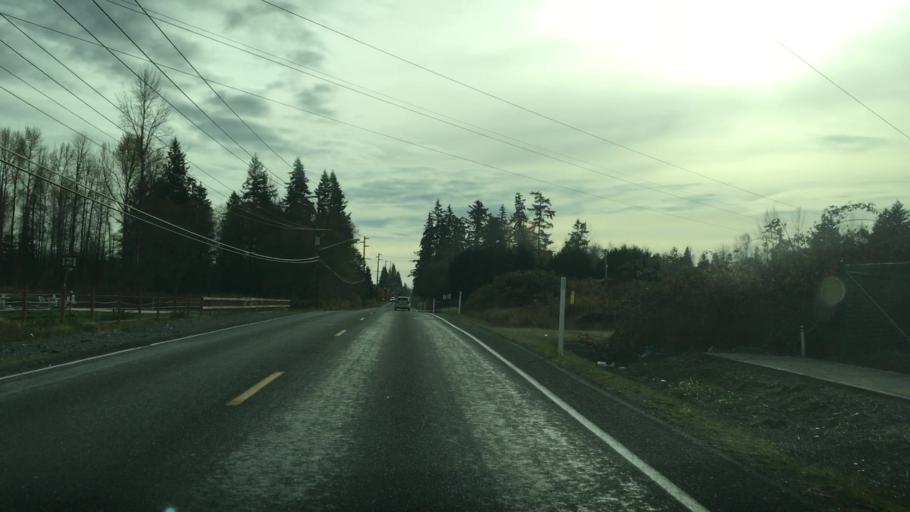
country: US
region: Washington
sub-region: Pierce County
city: South Hill
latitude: 47.1312
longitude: -122.3149
